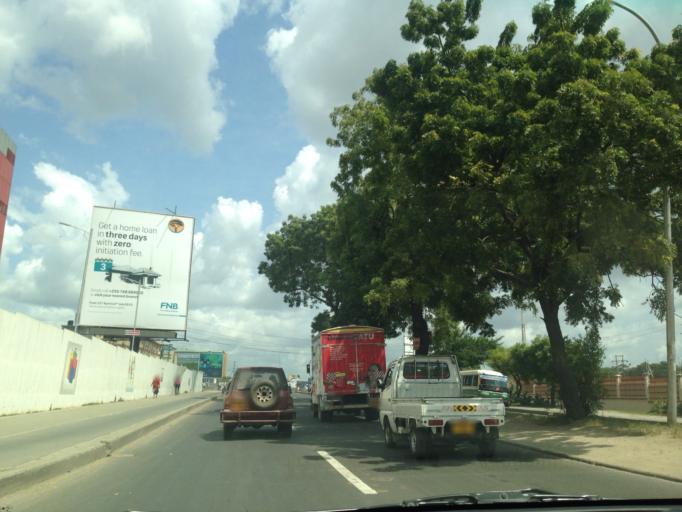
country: TZ
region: Dar es Salaam
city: Dar es Salaam
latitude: -6.8291
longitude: 39.2738
